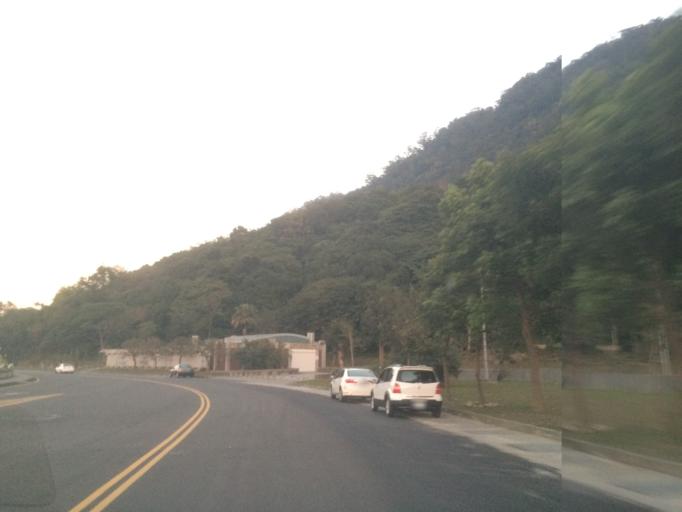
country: TW
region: Taiwan
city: Daxi
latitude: 24.8180
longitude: 121.2519
